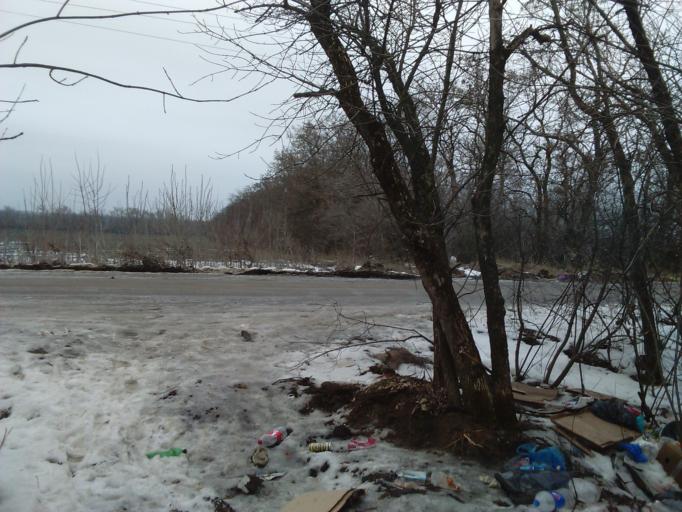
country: RU
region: Rostov
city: Temernik
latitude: 47.3552
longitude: 39.7398
